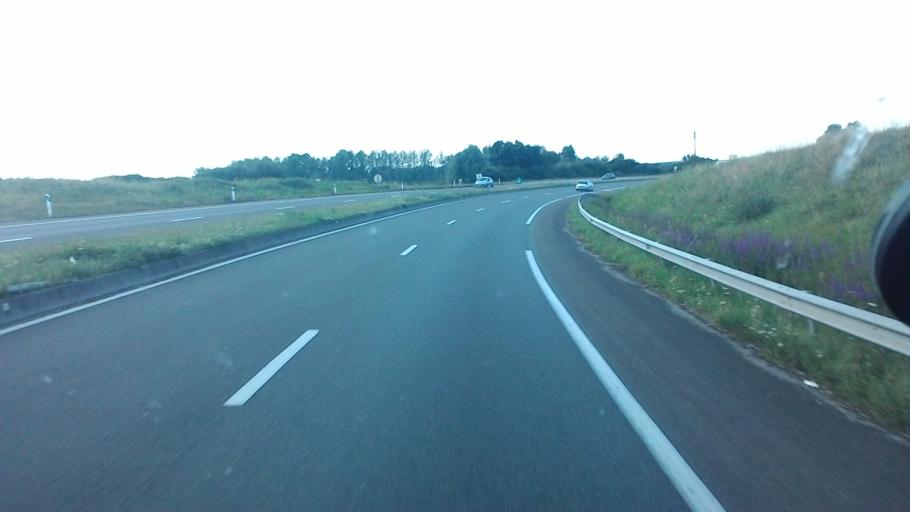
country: FR
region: Franche-Comte
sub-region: Departement de la Haute-Saone
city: Pusey
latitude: 47.6351
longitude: 6.1358
